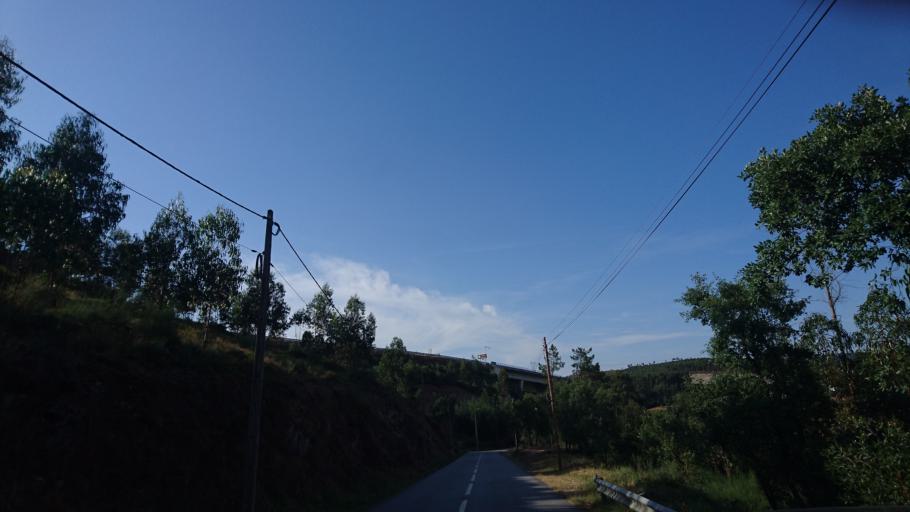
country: PT
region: Porto
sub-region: Paredes
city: Recarei
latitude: 41.1313
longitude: -8.4266
